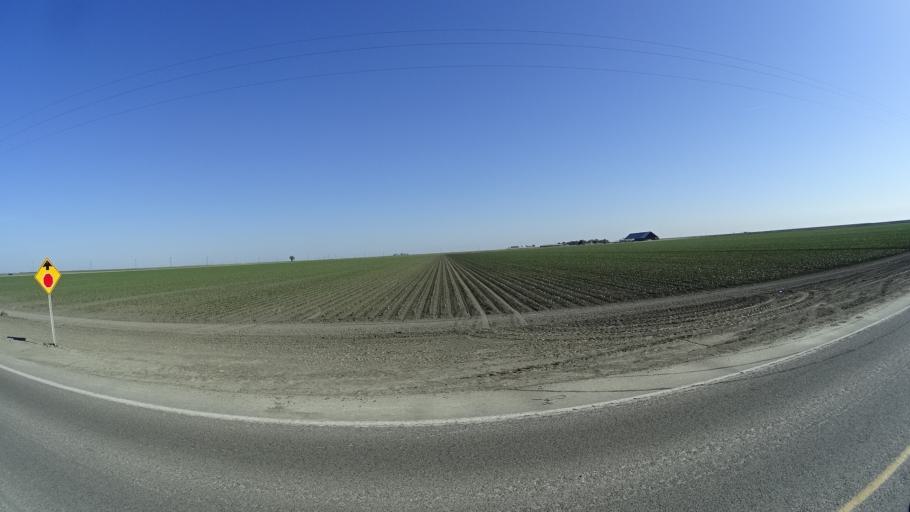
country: US
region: California
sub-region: Kings County
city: Corcoran
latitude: 36.0979
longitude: -119.6410
